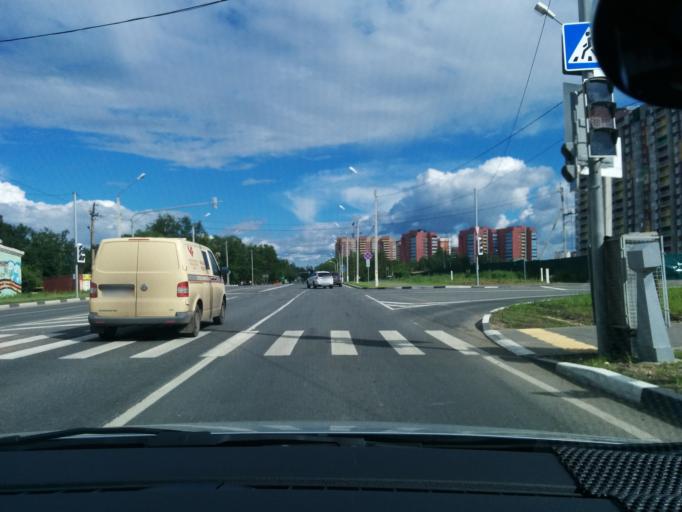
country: RU
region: Moskovskaya
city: Lobnya
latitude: 56.0261
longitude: 37.4707
